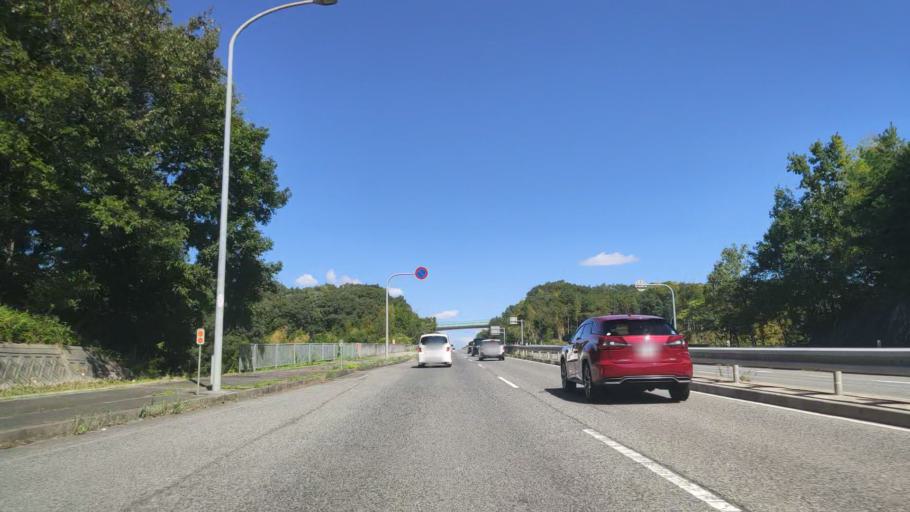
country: JP
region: Hyogo
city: Ono
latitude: 34.8237
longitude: 134.9503
